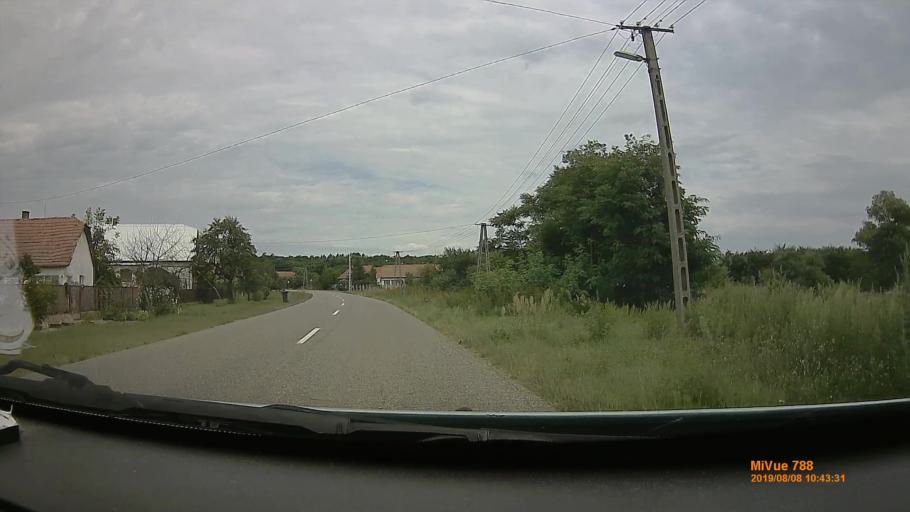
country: HU
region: Hajdu-Bihar
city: Nyiradony
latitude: 47.7229
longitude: 21.8770
